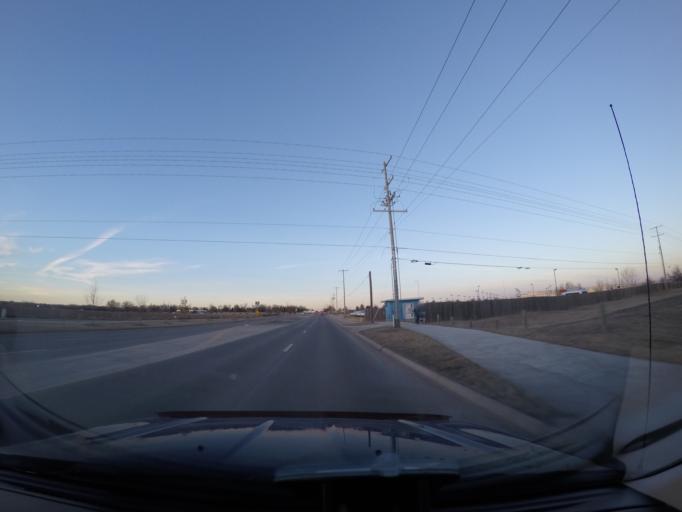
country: US
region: Kansas
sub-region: Sedgwick County
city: Goddard
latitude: 37.6605
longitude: -97.4806
